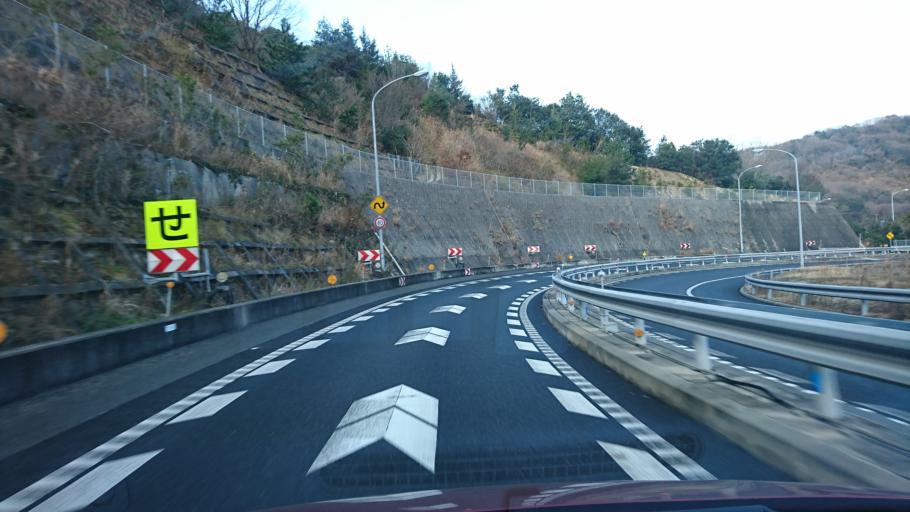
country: JP
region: Hyogo
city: Himeji
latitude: 34.8504
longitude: 134.7396
